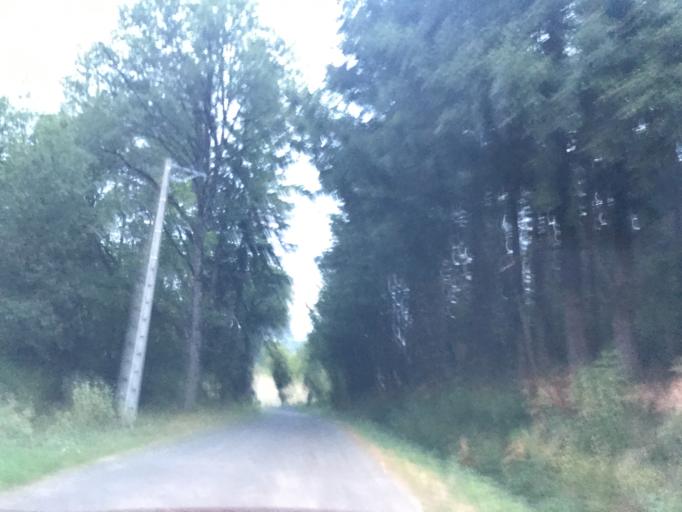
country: FR
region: Auvergne
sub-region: Departement du Puy-de-Dome
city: Escoutoux
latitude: 45.8024
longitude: 3.5671
